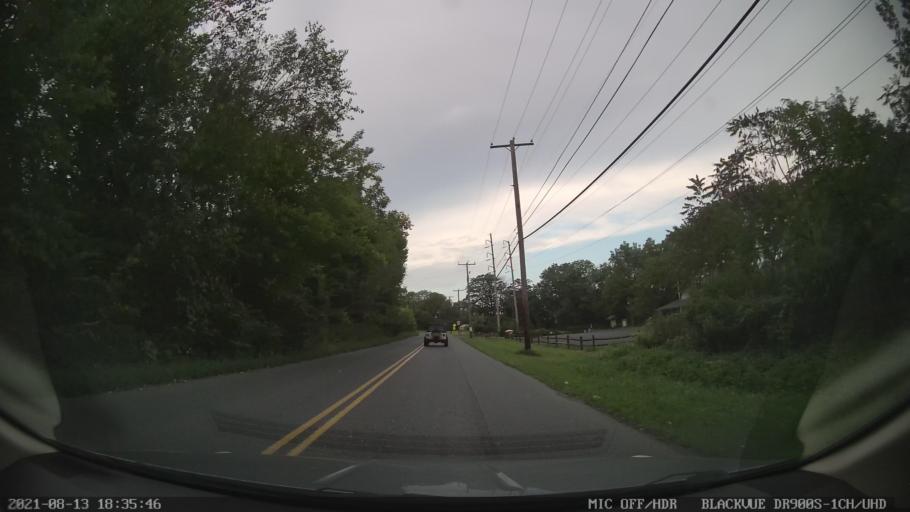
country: US
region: Pennsylvania
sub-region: Lehigh County
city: Stiles
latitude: 40.6710
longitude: -75.5090
